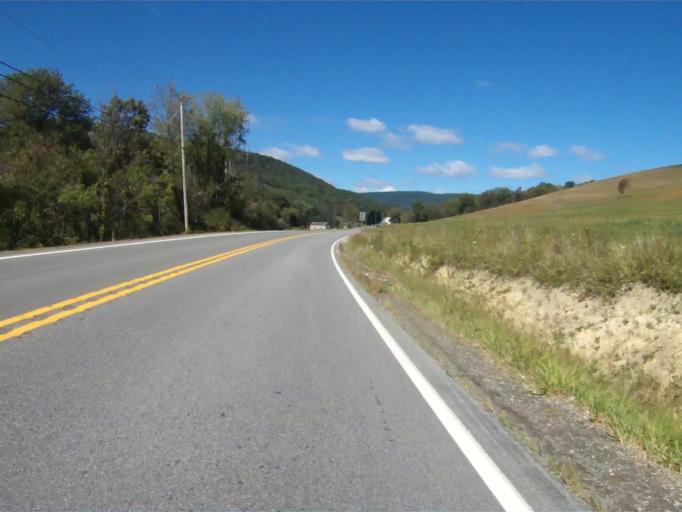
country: US
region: Pennsylvania
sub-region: Centre County
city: Houserville
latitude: 40.9095
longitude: -77.8820
